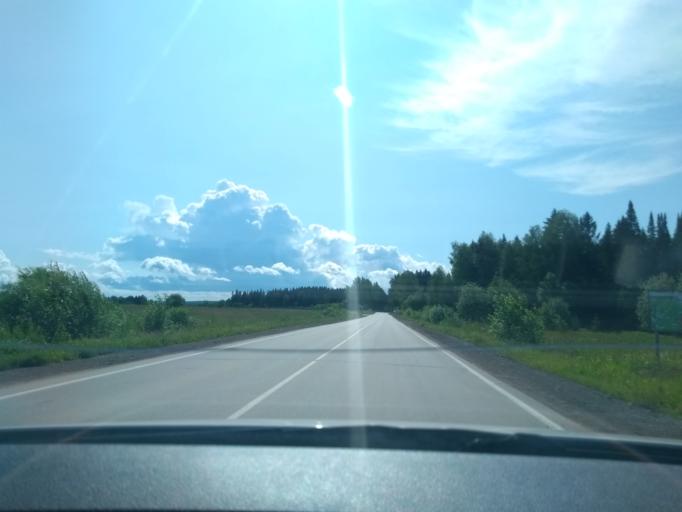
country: RU
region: Perm
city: Lobanovo
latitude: 57.8364
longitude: 56.3967
